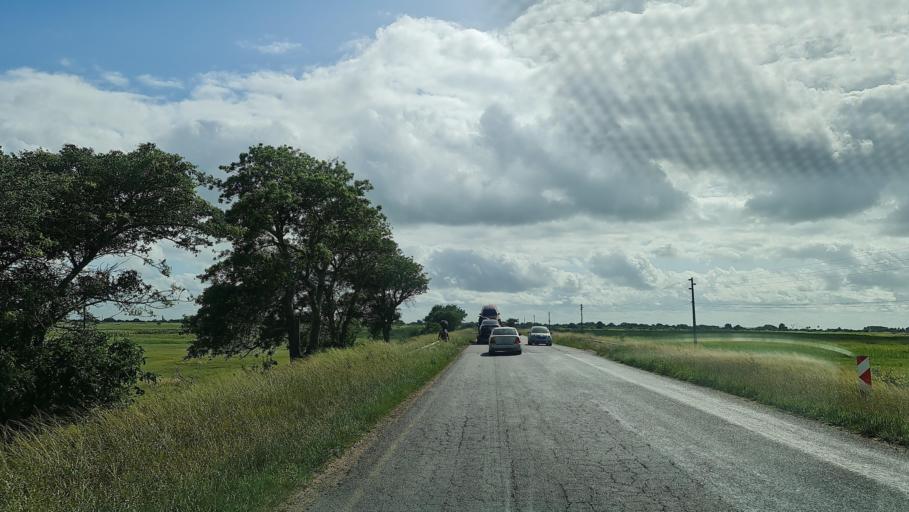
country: MZ
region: Gaza
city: Macia
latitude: -25.0963
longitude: 32.8305
